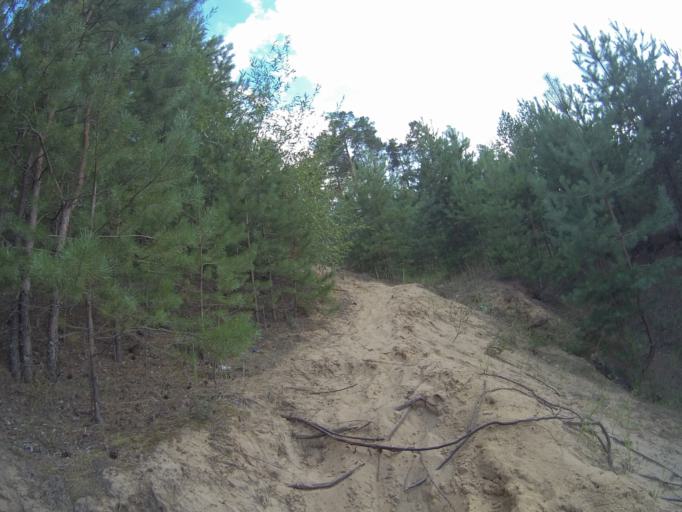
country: RU
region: Vladimir
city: Kommunar
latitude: 56.0399
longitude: 40.4278
